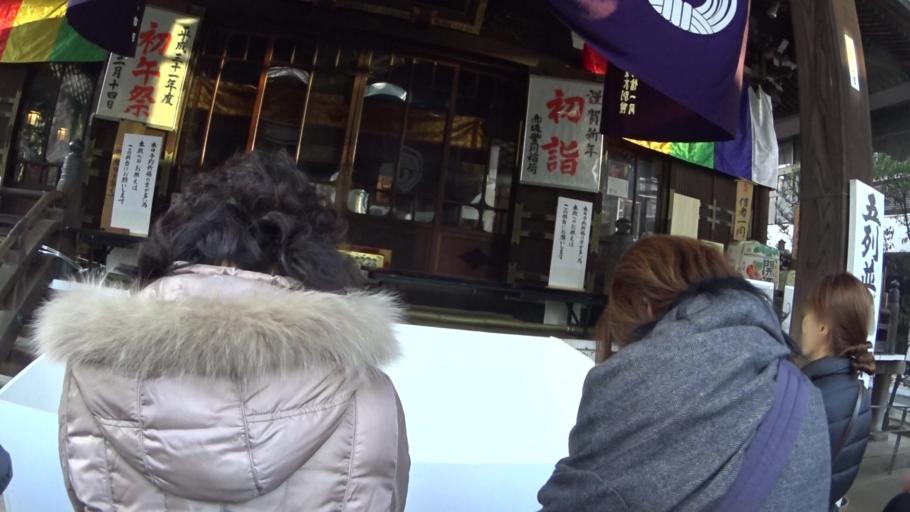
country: JP
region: Tokyo
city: Tokyo
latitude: 35.6751
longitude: 139.7329
